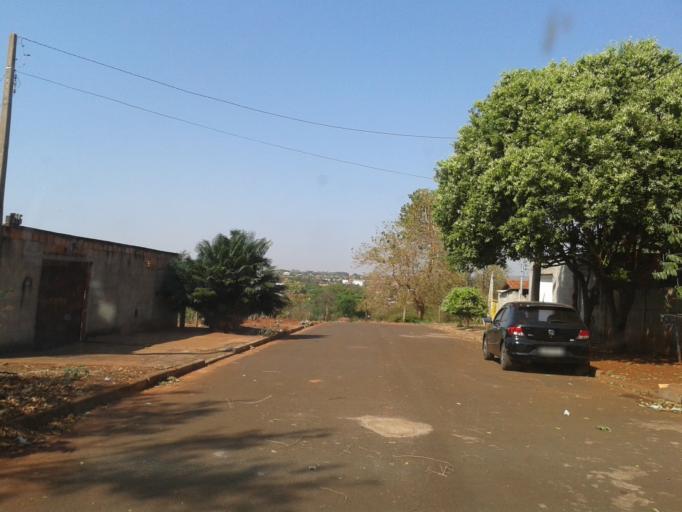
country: BR
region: Minas Gerais
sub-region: Ituiutaba
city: Ituiutaba
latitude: -18.9631
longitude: -49.4829
